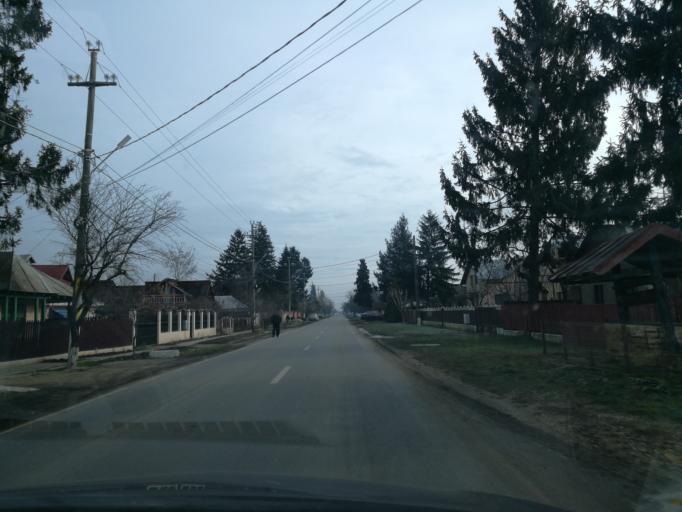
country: RO
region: Ilfov
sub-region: Comuna Moara Vlasiei
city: Caciulati
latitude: 44.6277
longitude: 26.1644
